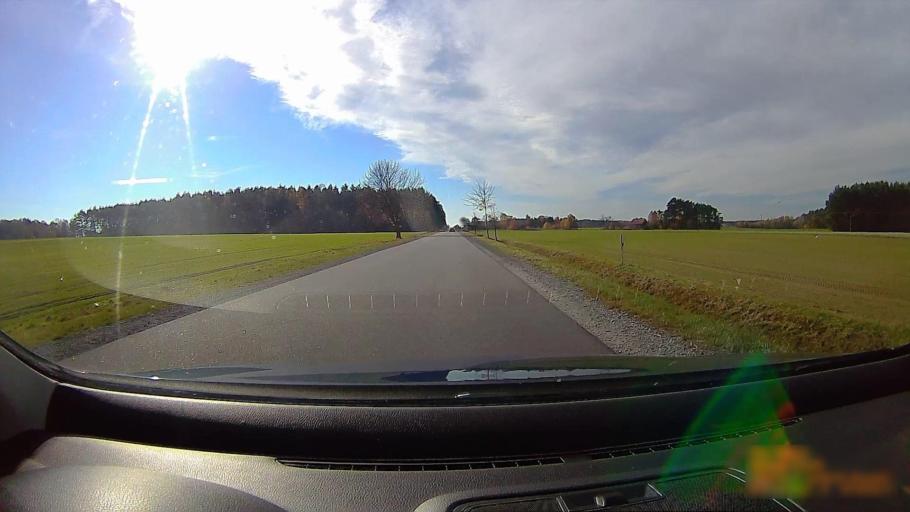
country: PL
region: Greater Poland Voivodeship
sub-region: Powiat ostrzeszowski
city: Doruchow
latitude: 51.3764
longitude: 18.0398
